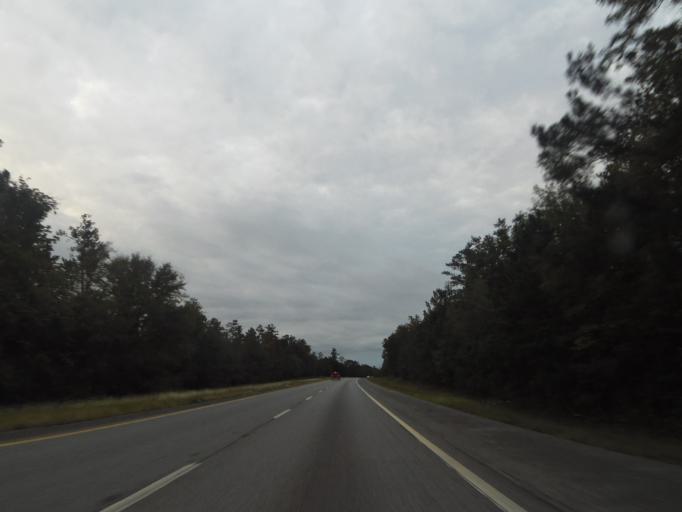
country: US
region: Alabama
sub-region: Saint Clair County
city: Steele
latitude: 33.9130
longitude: -86.2185
